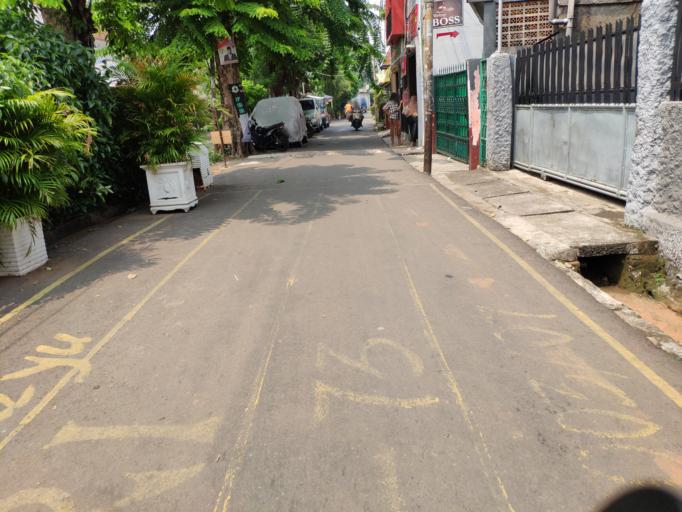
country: ID
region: Jakarta Raya
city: Jakarta
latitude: -6.2025
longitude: 106.8593
